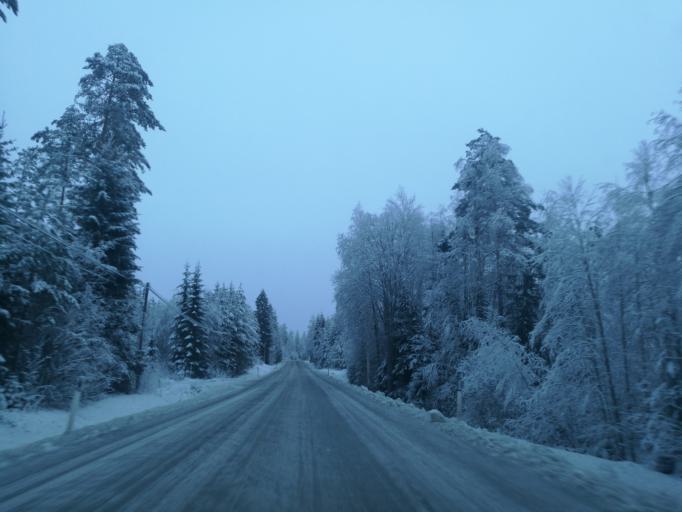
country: NO
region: Hedmark
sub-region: Grue
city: Kirkenaer
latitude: 60.3004
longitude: 12.2479
